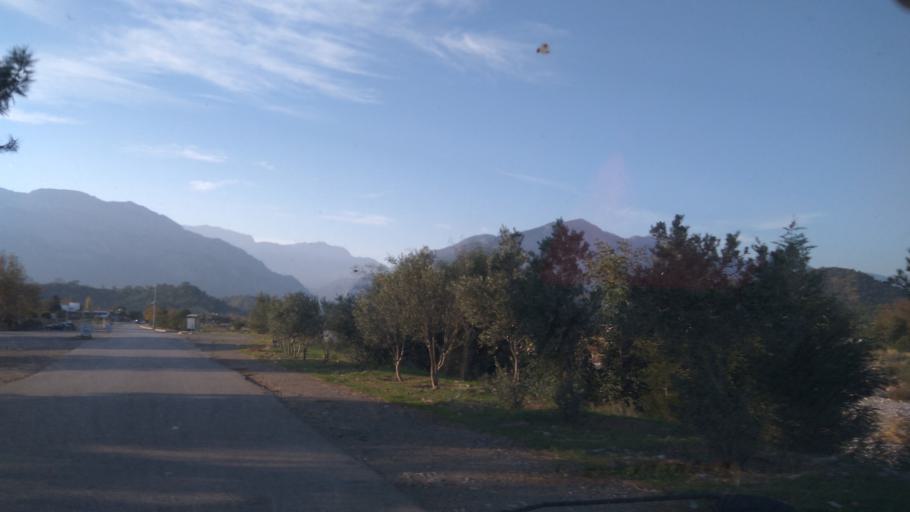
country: TR
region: Antalya
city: Kemer
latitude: 36.5661
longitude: 30.5683
